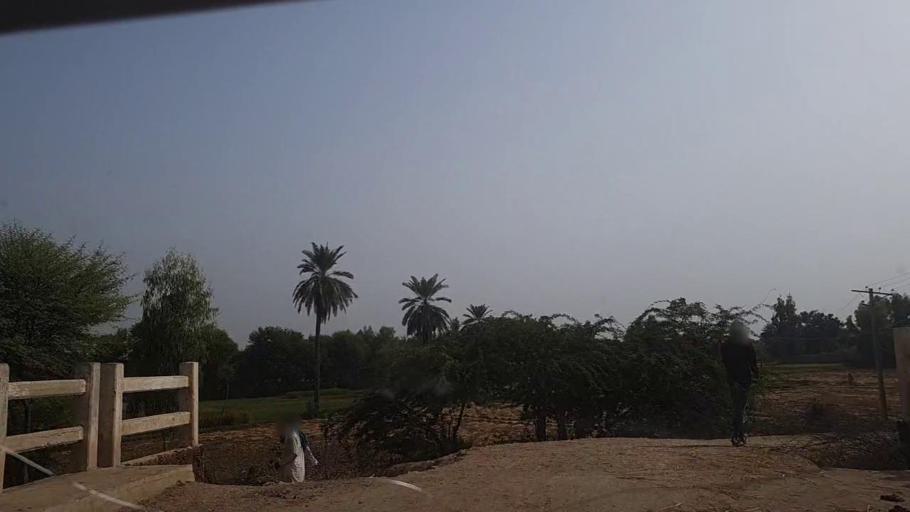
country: PK
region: Sindh
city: Madeji
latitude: 27.7325
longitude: 68.4364
